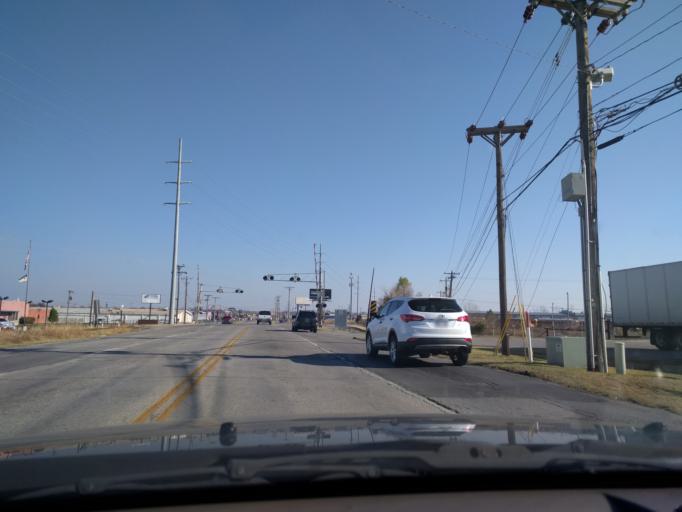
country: US
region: Oklahoma
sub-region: Tulsa County
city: Jenks
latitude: 36.1044
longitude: -95.8923
